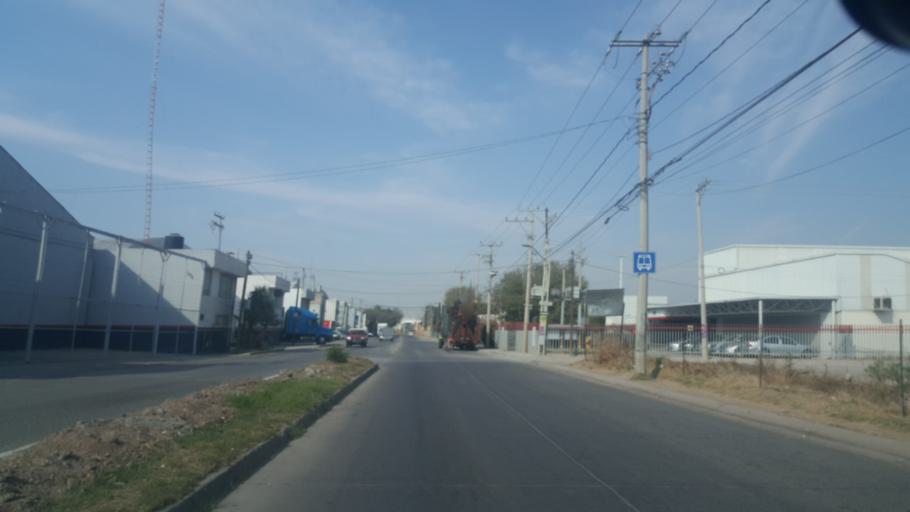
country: MX
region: Guanajuato
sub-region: Leon
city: Fraccionamiento Paraiso Real
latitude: 21.1041
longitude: -101.6196
